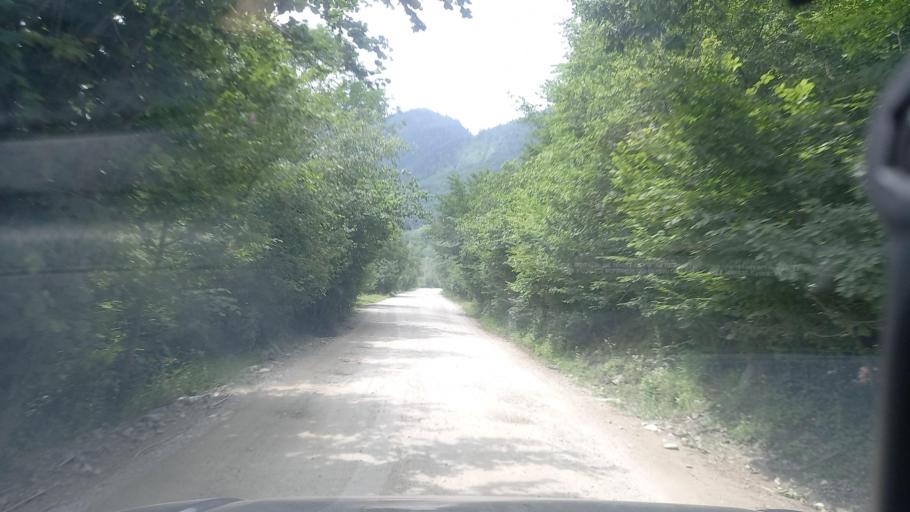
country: RU
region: Karachayevo-Cherkesiya
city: Kurdzhinovo
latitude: 43.9067
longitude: 40.9530
